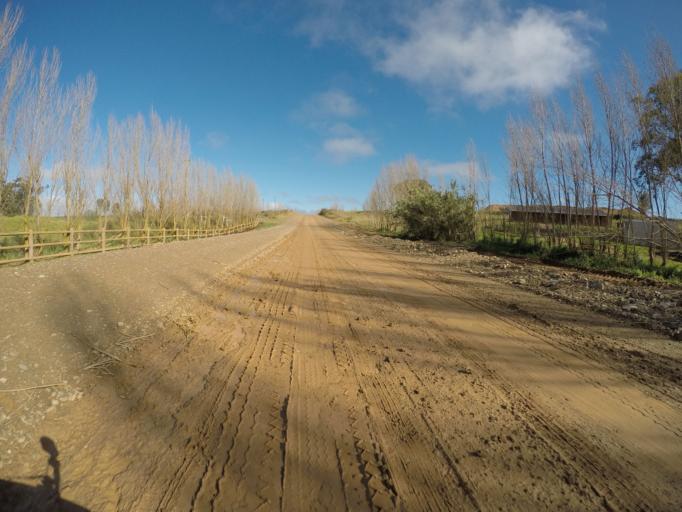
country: ZA
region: Western Cape
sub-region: Overberg District Municipality
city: Caledon
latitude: -34.1127
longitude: 19.7450
